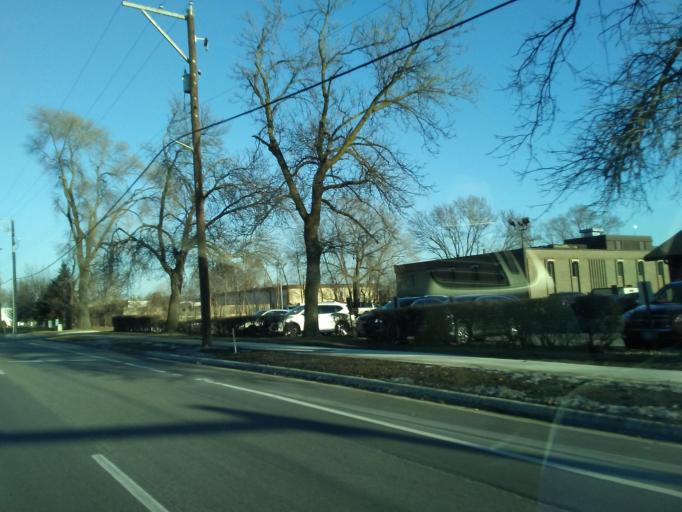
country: US
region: Minnesota
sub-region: Hennepin County
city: Bloomington
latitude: 44.8479
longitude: -93.2882
